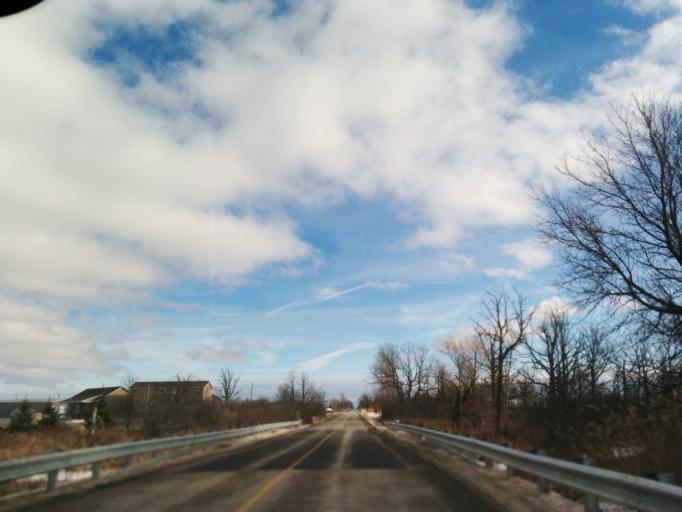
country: CA
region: Ontario
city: Brantford
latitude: 42.9904
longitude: -80.0729
